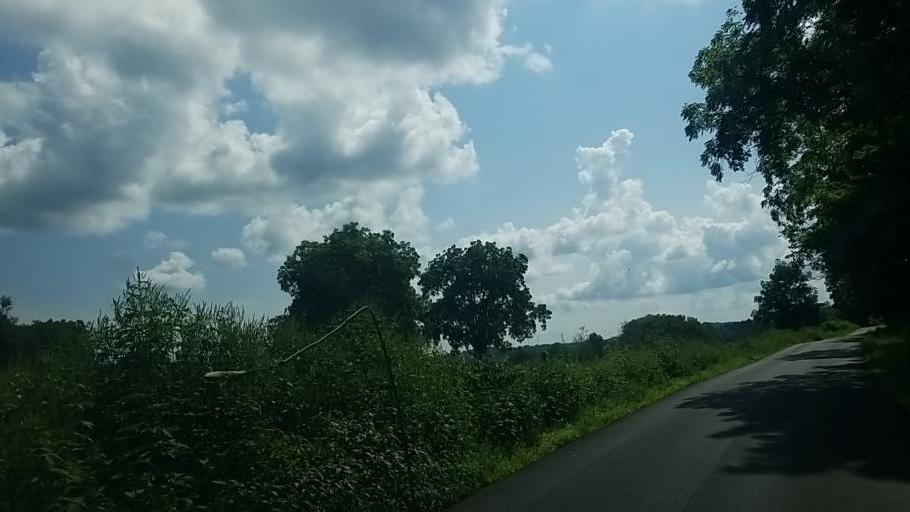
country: US
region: Ohio
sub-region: Richland County
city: Lincoln Heights
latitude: 40.6862
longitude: -82.3832
